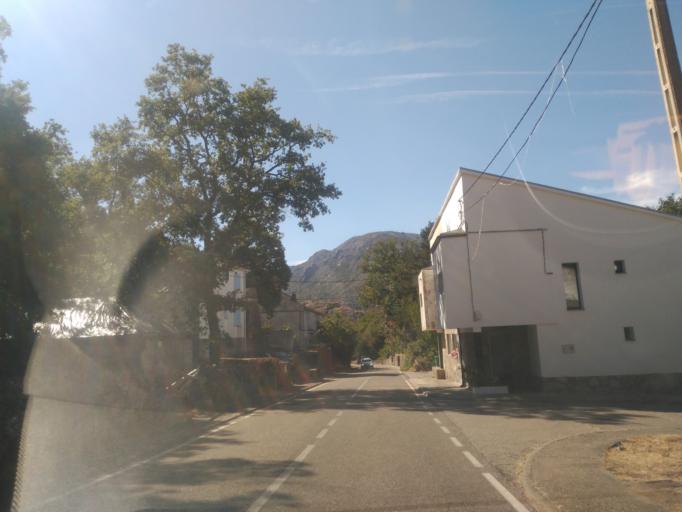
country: ES
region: Castille and Leon
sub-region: Provincia de Zamora
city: Cobreros
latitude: 42.1148
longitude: -6.7402
